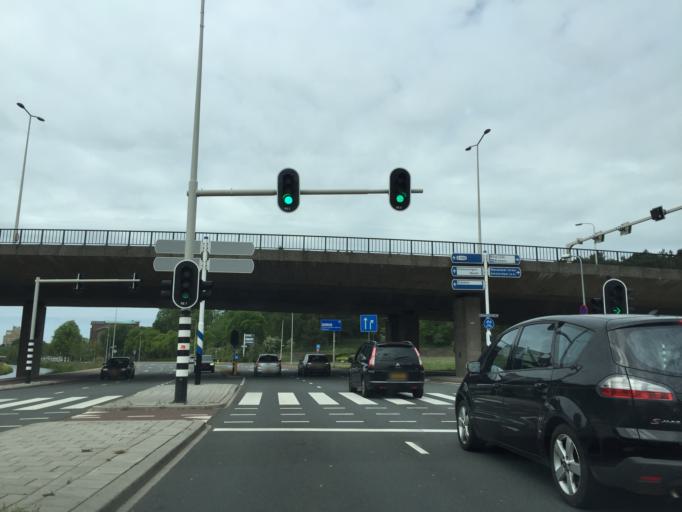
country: NL
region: South Holland
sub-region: Gemeente Den Haag
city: The Hague
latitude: 52.0963
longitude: 4.3073
